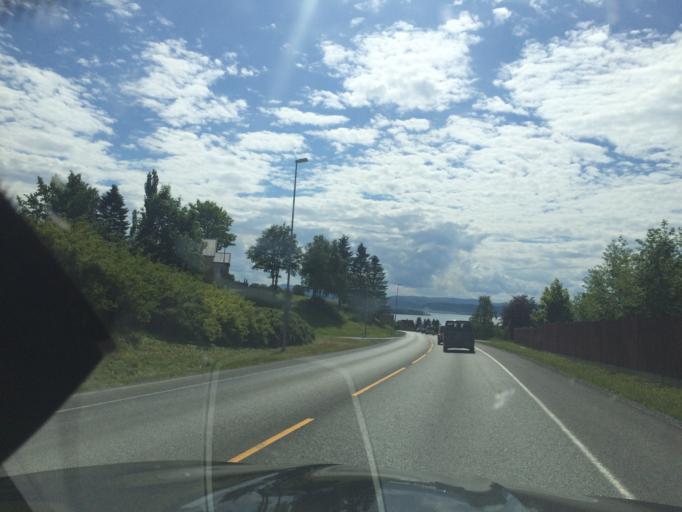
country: NO
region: Nord-Trondelag
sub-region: Inderoy
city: Straumen
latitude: 63.8568
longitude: 11.3982
